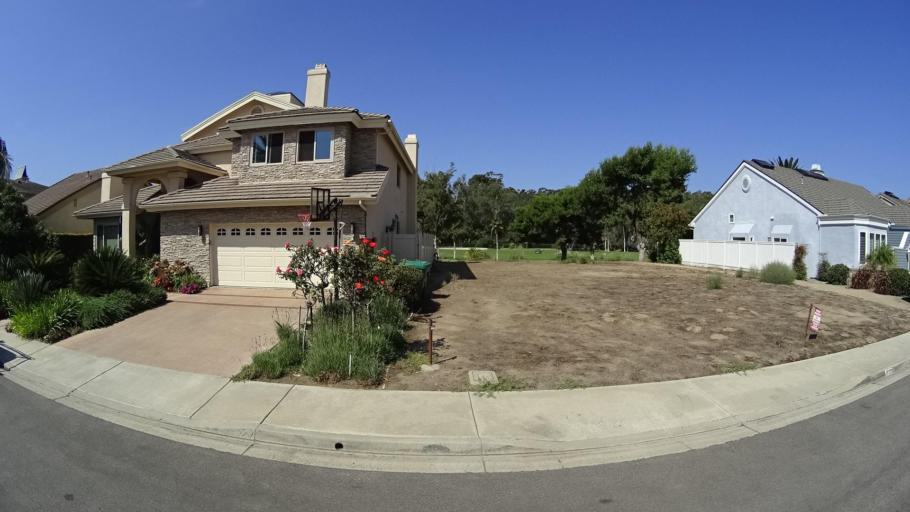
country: US
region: California
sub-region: San Diego County
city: Fairbanks Ranch
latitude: 32.9878
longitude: -117.2148
